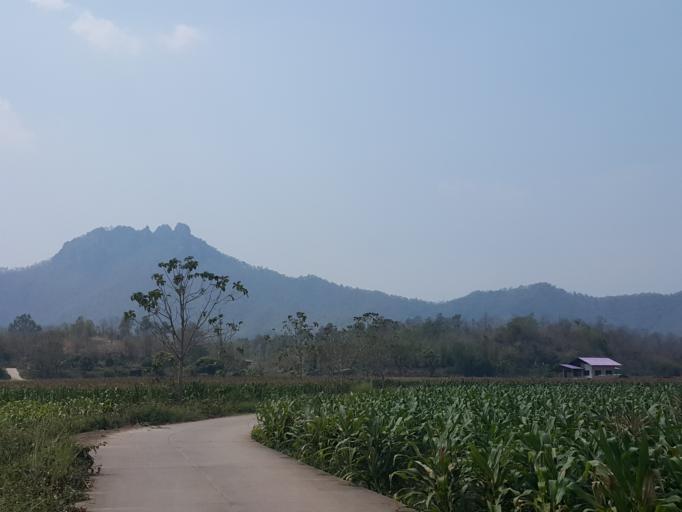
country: TH
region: Lampang
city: Chae Hom
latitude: 18.7471
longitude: 99.5628
